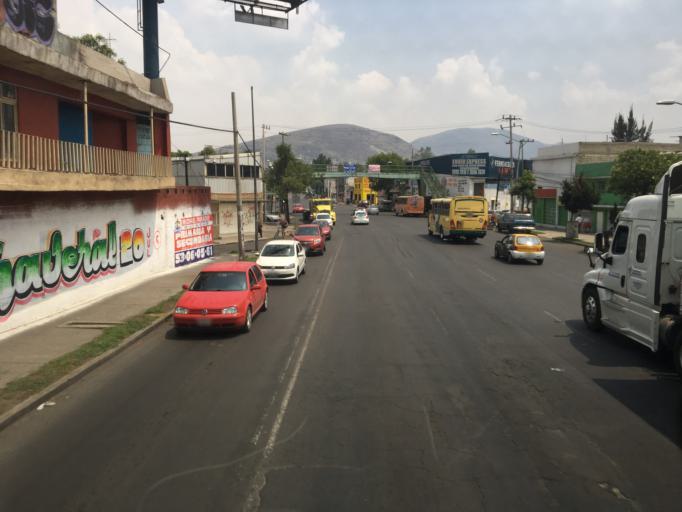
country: MX
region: Mexico
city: Tlalnepantla
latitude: 19.5223
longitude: -99.1579
